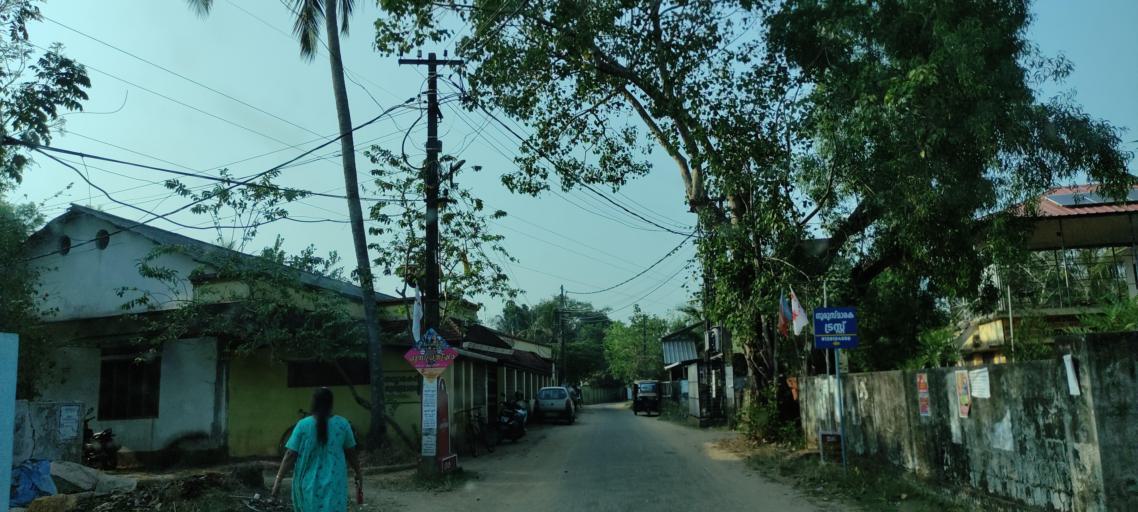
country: IN
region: Kerala
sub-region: Alappuzha
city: Alleppey
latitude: 9.5222
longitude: 76.3223
